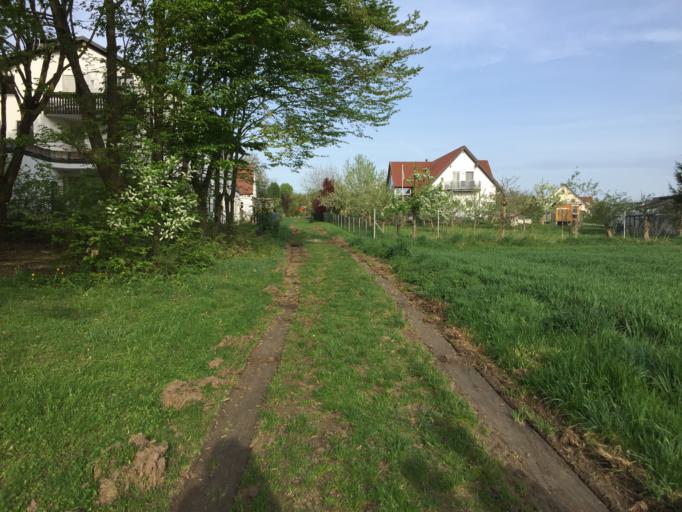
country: DE
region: Bavaria
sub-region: Swabia
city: Wertingen
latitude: 48.5675
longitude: 10.6797
